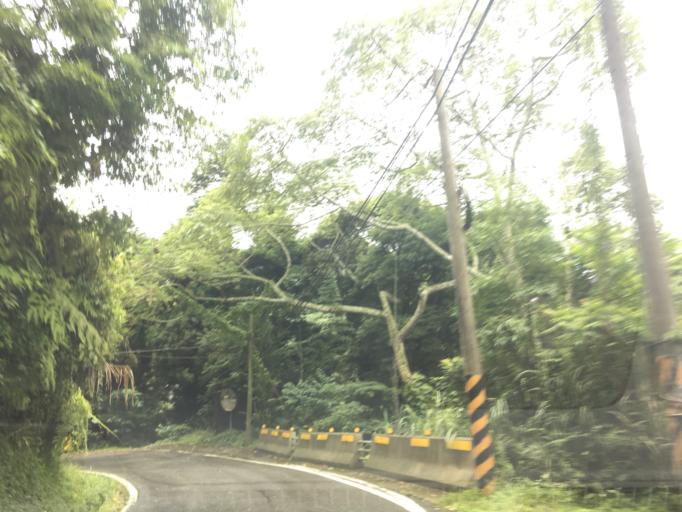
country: TW
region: Taiwan
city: Lugu
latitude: 23.5483
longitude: 120.6831
